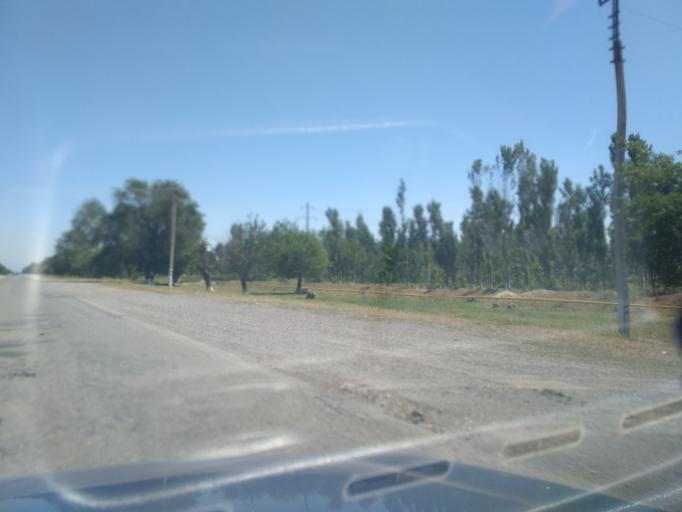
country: TJ
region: Viloyati Sughd
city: Zafarobod
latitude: 40.2224
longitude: 68.9302
